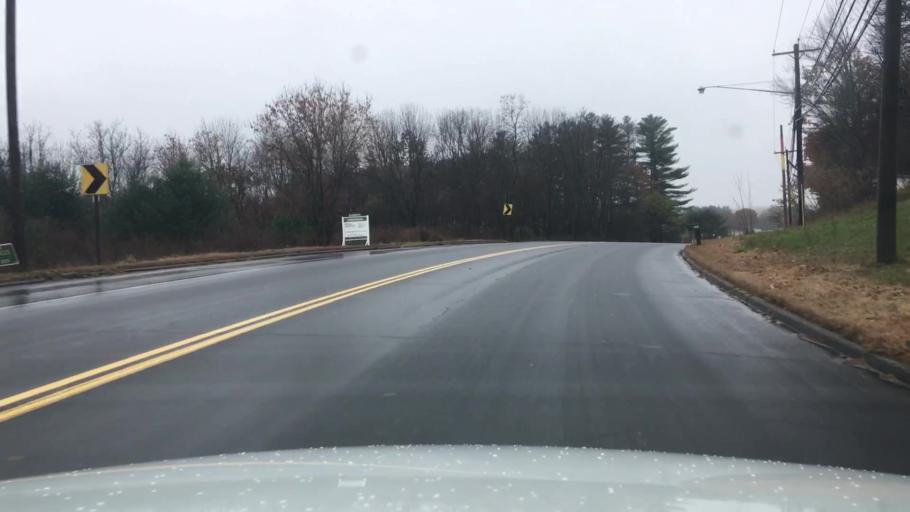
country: US
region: Maine
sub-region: Androscoggin County
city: Sabattus
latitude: 44.1000
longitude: -70.1476
